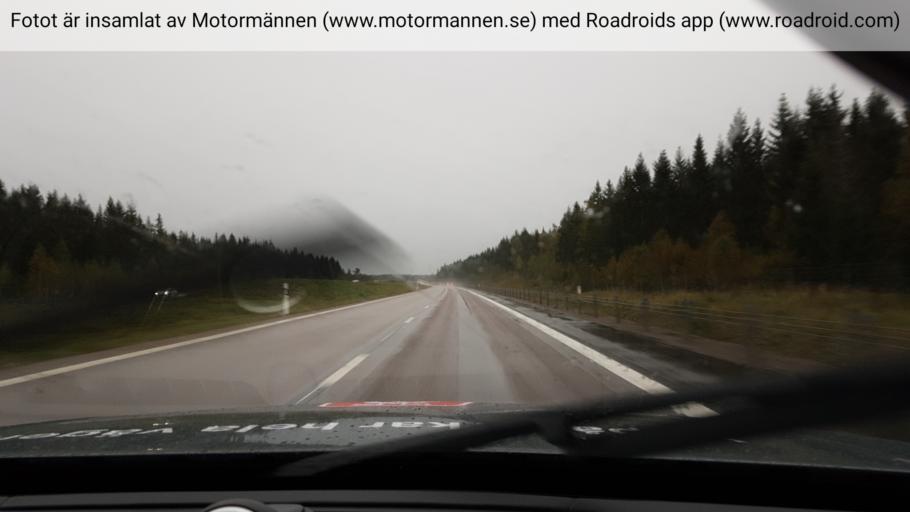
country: SE
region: Uppsala
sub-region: Tierps Kommun
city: Tierp
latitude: 60.4196
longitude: 17.4443
